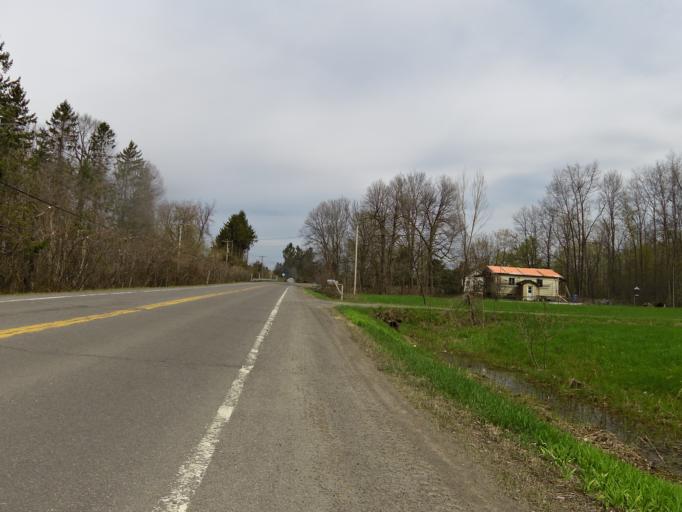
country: CA
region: Quebec
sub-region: Monteregie
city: Hudson
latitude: 45.4748
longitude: -74.1264
